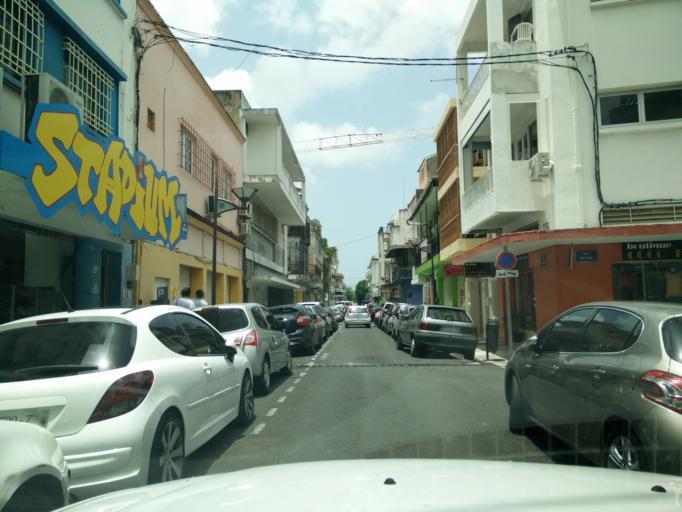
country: GP
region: Guadeloupe
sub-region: Guadeloupe
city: Pointe-a-Pitre
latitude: 16.2363
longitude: -61.5376
